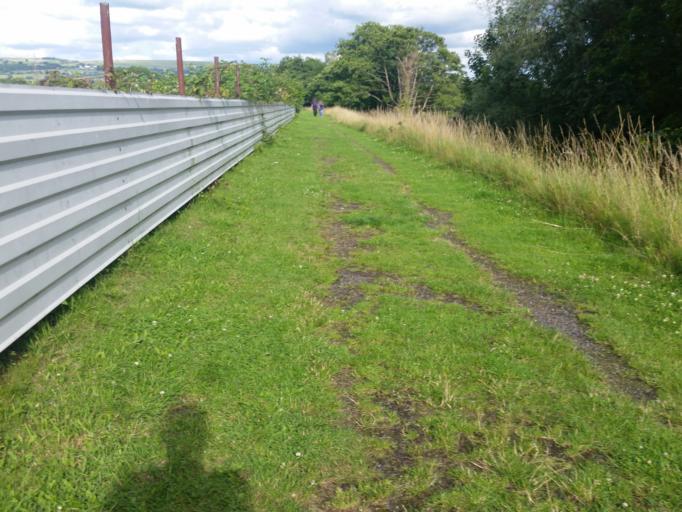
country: GB
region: Wales
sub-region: City and County of Swansea
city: Clydach
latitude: 51.6741
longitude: -3.9118
